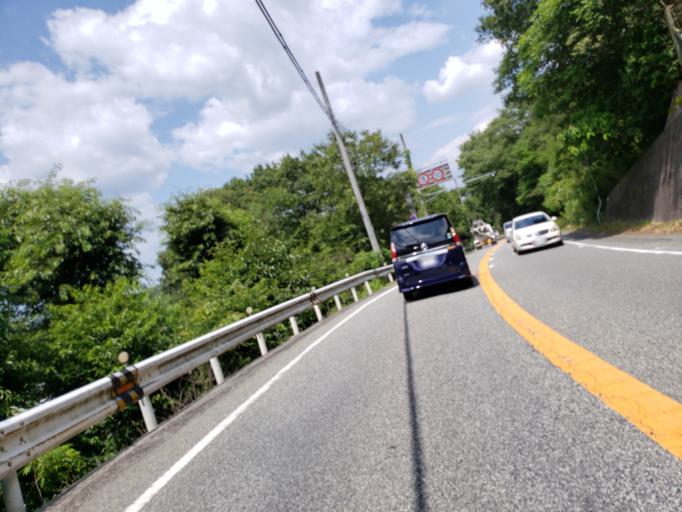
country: JP
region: Hyogo
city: Aioi
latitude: 34.7995
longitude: 134.4500
